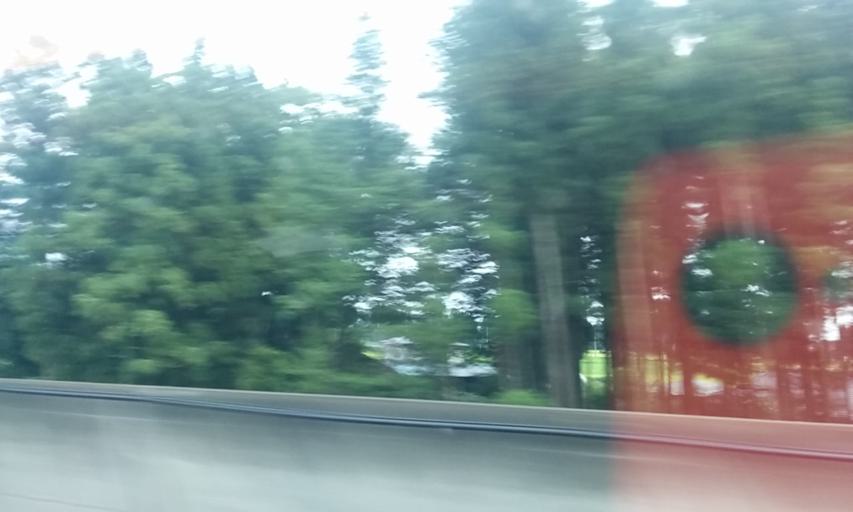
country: JP
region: Tochigi
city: Kuroiso
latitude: 37.0289
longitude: 140.1063
